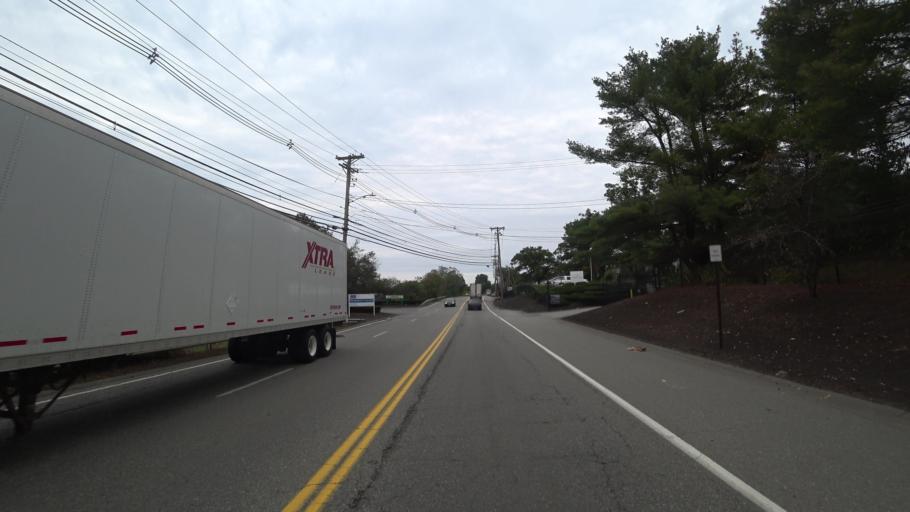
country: US
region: Massachusetts
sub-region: Middlesex County
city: Wilmington
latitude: 42.5927
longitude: -71.1610
